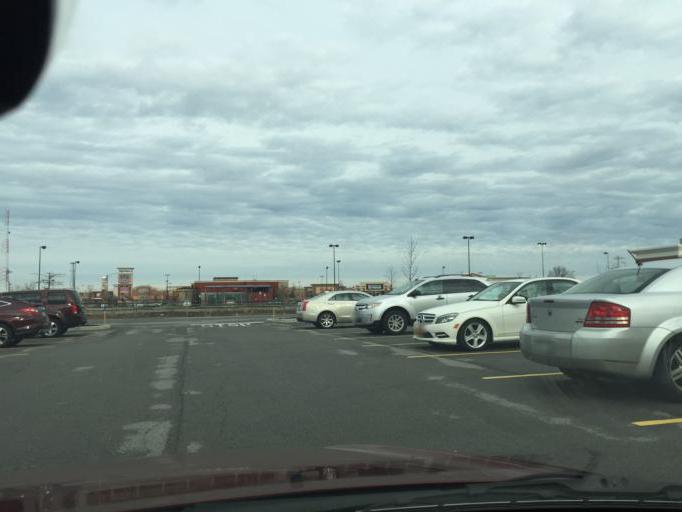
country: US
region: New York
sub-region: Monroe County
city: Rochester
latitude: 43.0851
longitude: -77.6242
